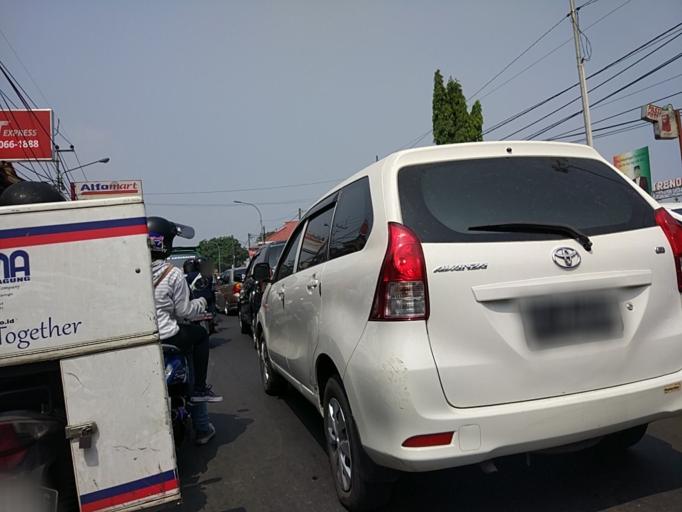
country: ID
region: West Java
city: Padalarang
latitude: -6.8555
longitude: 107.4983
